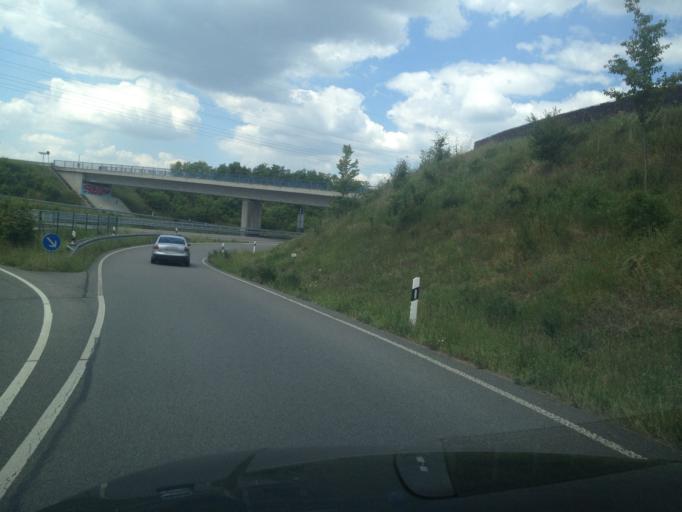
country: DE
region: Baden-Wuerttemberg
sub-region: Karlsruhe Region
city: Schwetzingen
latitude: 49.3924
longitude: 8.5822
